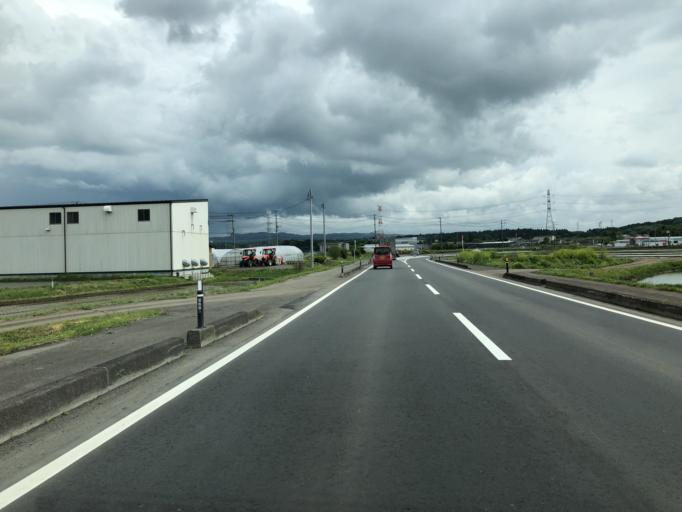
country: JP
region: Fukushima
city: Ishikawa
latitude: 37.0662
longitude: 140.3719
